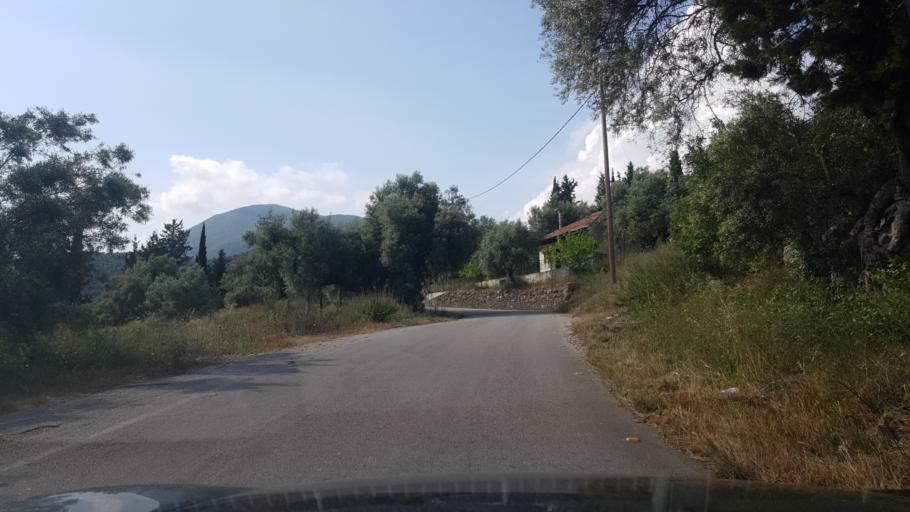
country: GR
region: Ionian Islands
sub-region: Lefkada
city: Nidri
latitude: 38.6415
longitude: 20.6985
